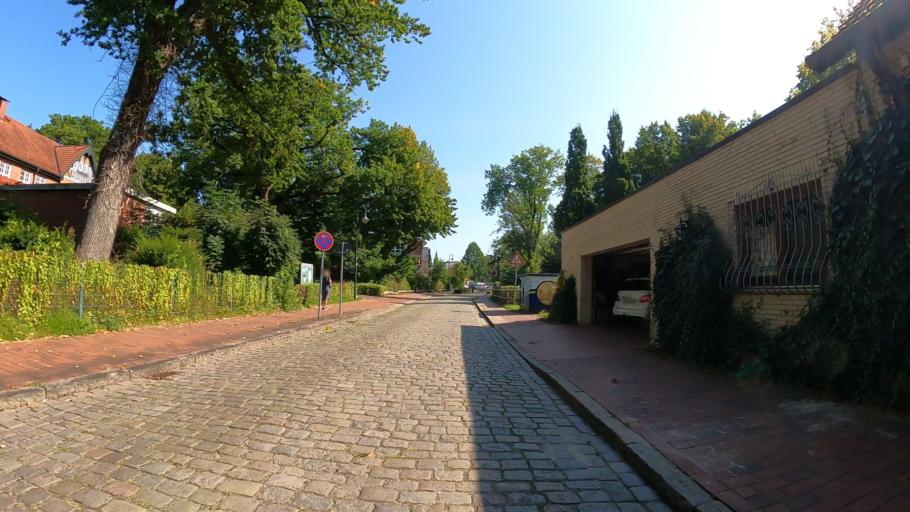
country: DE
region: Schleswig-Holstein
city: Bad Bramstedt
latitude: 53.9200
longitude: 9.8831
